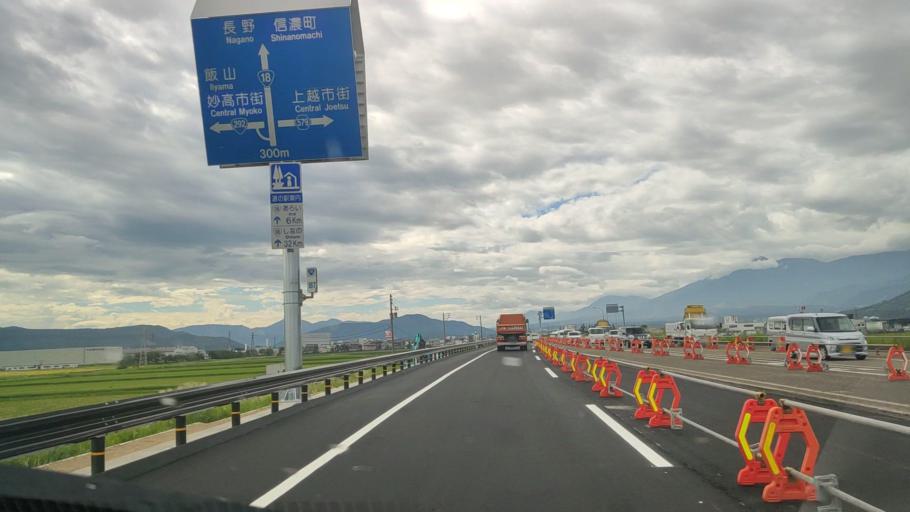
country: JP
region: Niigata
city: Arai
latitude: 37.0644
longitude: 138.2629
